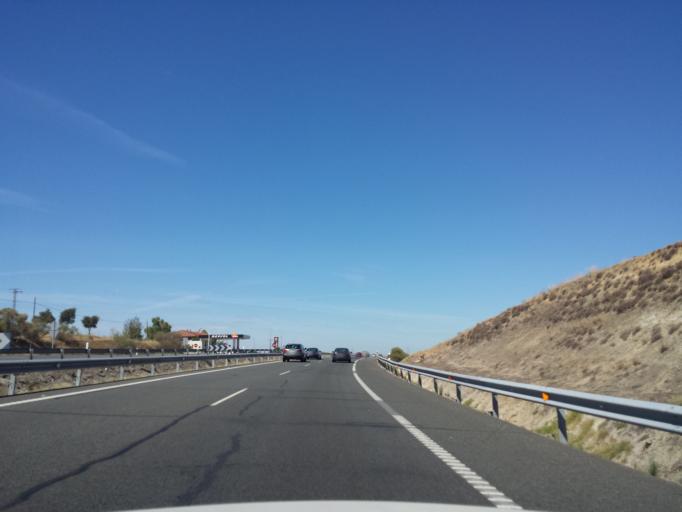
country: ES
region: Castille-La Mancha
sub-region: Province of Toledo
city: Caleruela
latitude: 39.8954
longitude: -5.3014
